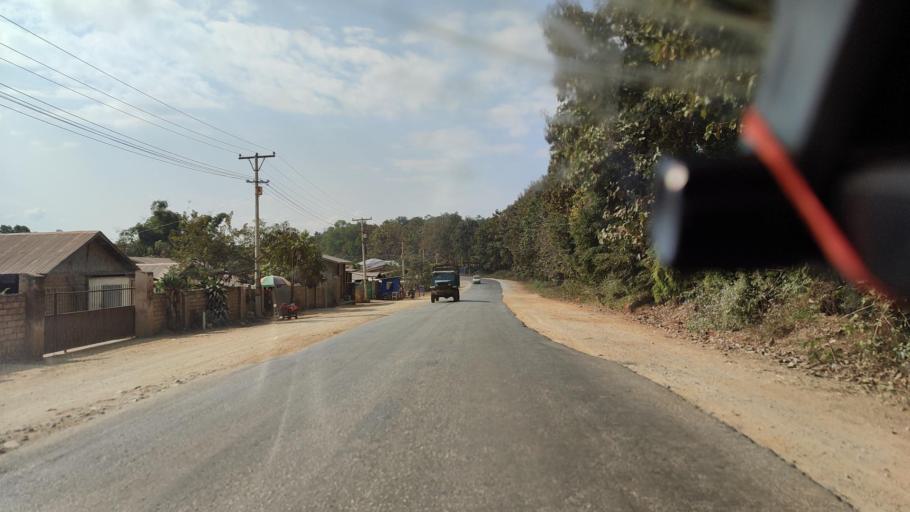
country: MM
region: Shan
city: Lashio
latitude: 23.2471
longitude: 97.9241
